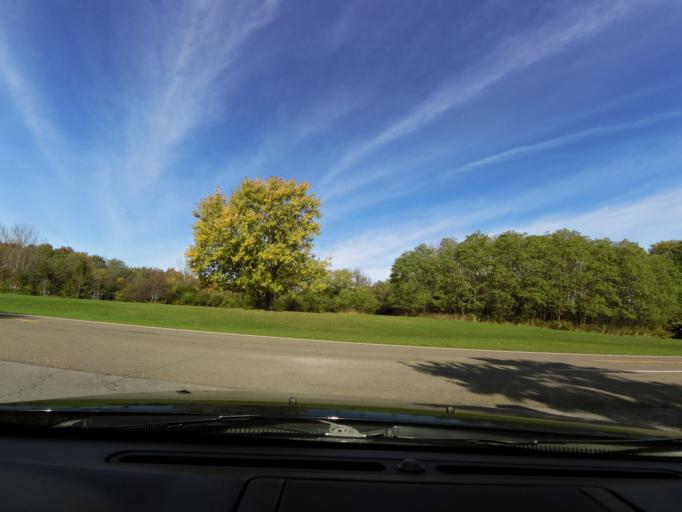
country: US
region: New York
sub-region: Livingston County
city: Mount Morris
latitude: 42.7355
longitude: -77.9079
